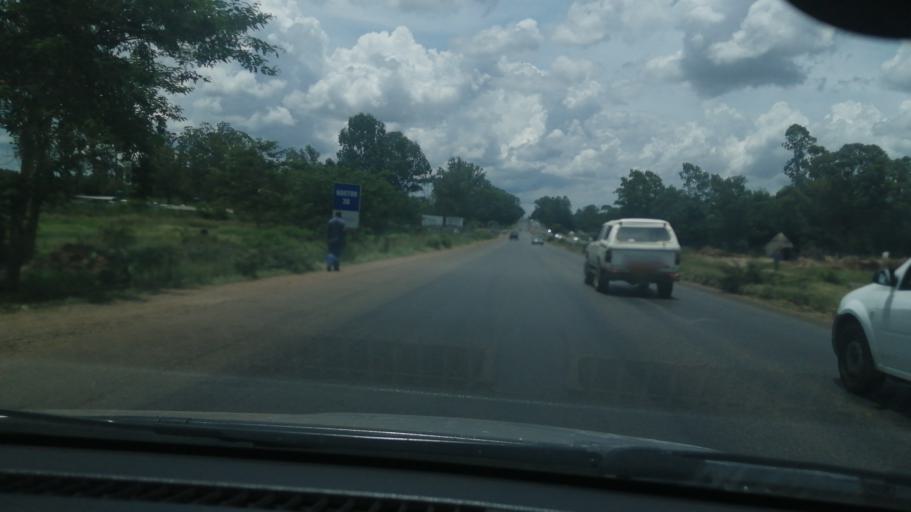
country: ZW
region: Harare
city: Harare
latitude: -17.8217
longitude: 30.9583
